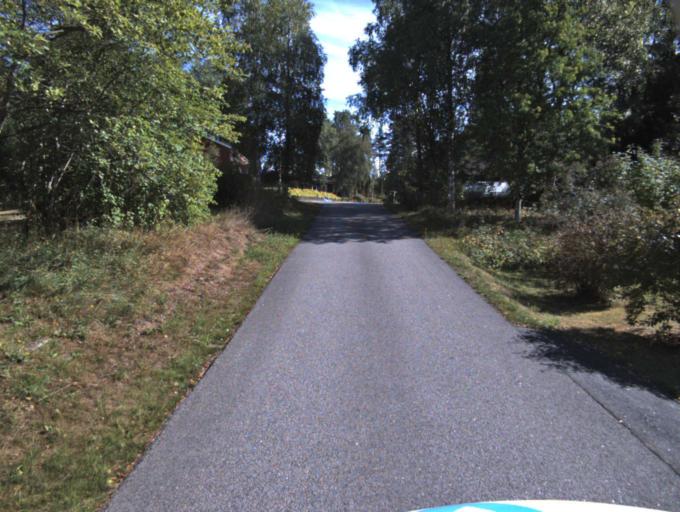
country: SE
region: Vaestra Goetaland
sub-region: Ulricehamns Kommun
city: Ulricehamn
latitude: 57.6938
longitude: 13.5766
